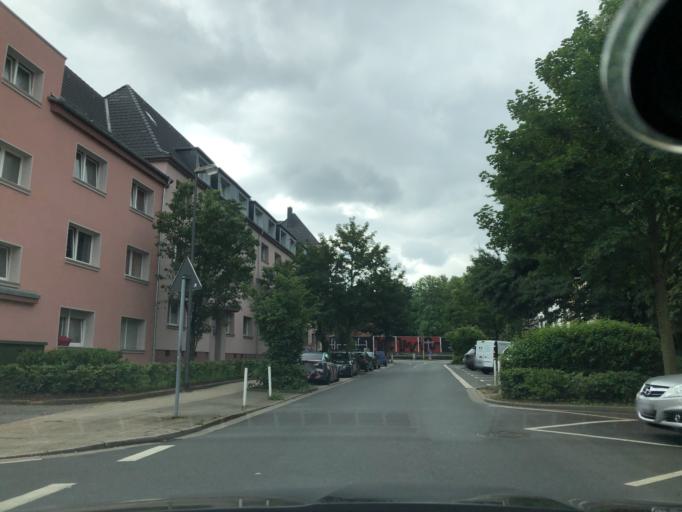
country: DE
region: North Rhine-Westphalia
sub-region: Regierungsbezirk Dusseldorf
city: Essen
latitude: 51.4546
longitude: 7.0343
